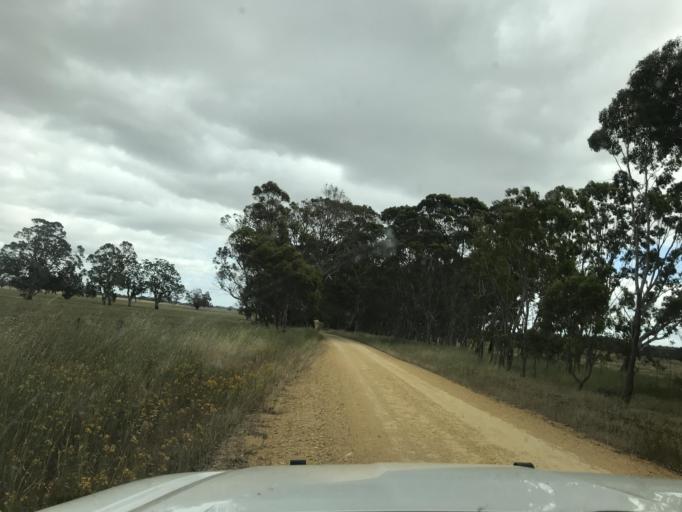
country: AU
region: South Australia
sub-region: Naracoorte and Lucindale
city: Naracoorte
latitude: -36.9469
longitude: 141.4184
